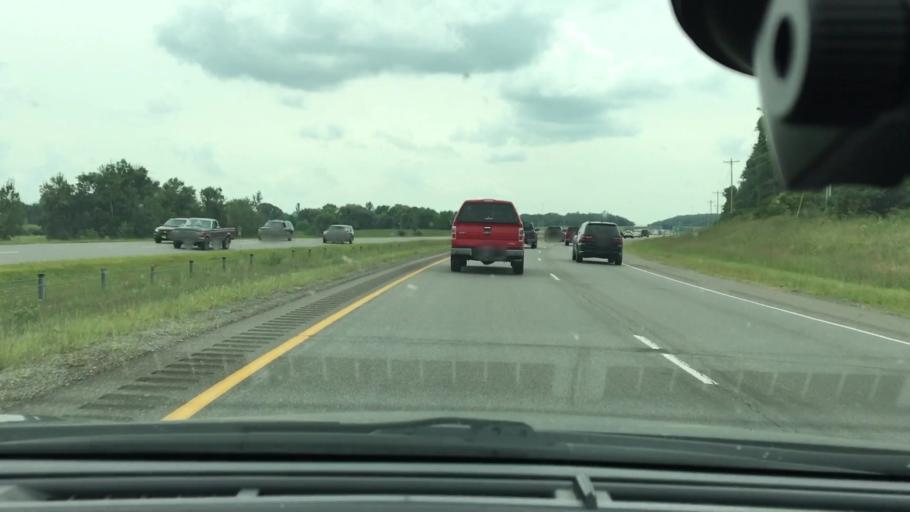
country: US
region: Minnesota
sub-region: Sherburne County
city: Elk River
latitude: 45.3510
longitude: -93.5583
